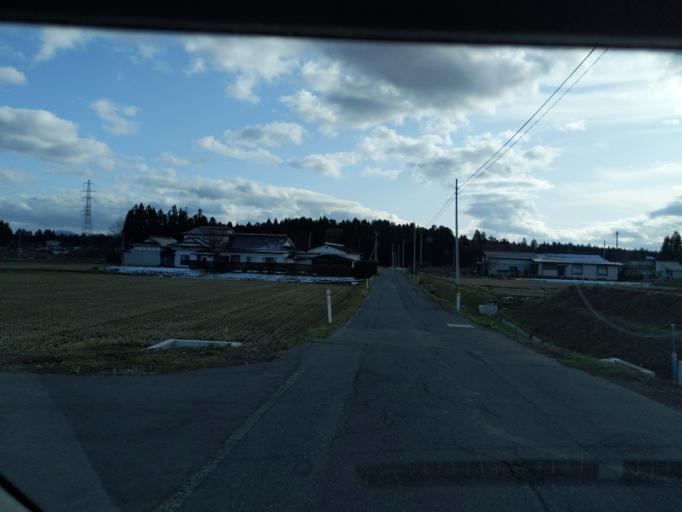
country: JP
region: Iwate
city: Mizusawa
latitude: 39.1188
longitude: 141.0822
